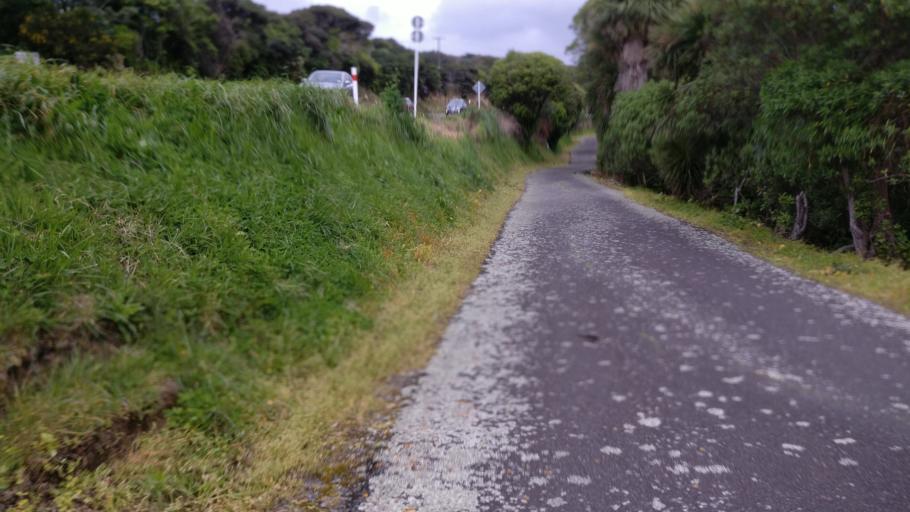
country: NZ
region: Wellington
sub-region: Porirua City
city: Porirua
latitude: -41.0427
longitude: 174.8840
